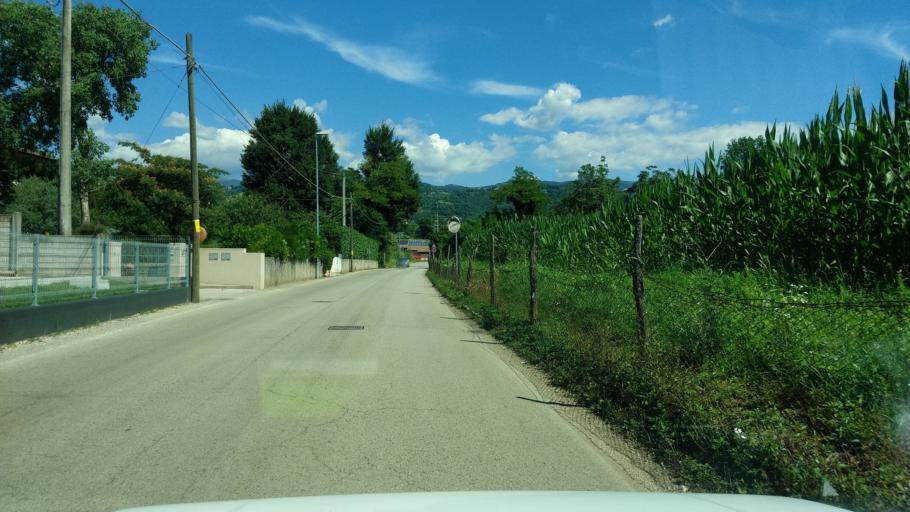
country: IT
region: Veneto
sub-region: Provincia di Vicenza
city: Pianezze
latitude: 45.7261
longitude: 11.6311
